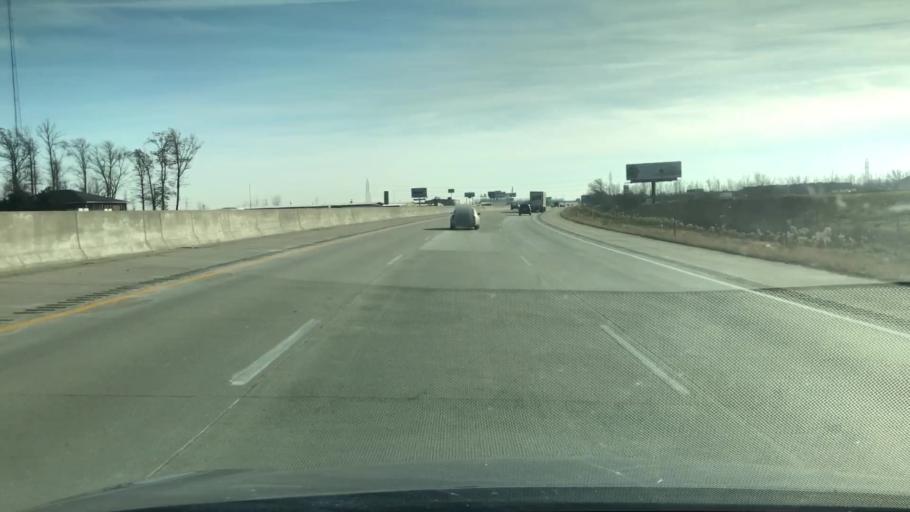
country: US
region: Michigan
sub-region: Saginaw County
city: Zilwaukee
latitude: 43.4628
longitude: -83.8923
